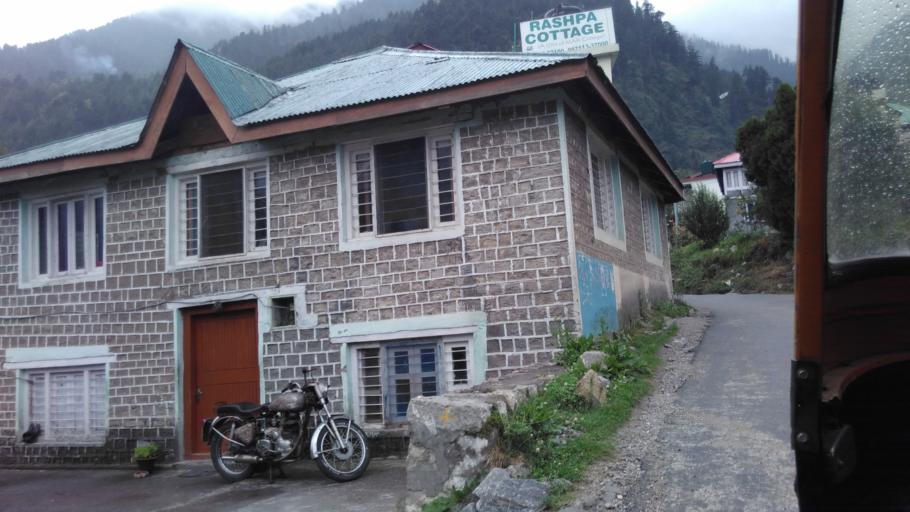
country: IN
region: Himachal Pradesh
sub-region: Kulu
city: Manali
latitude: 32.2196
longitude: 77.1872
